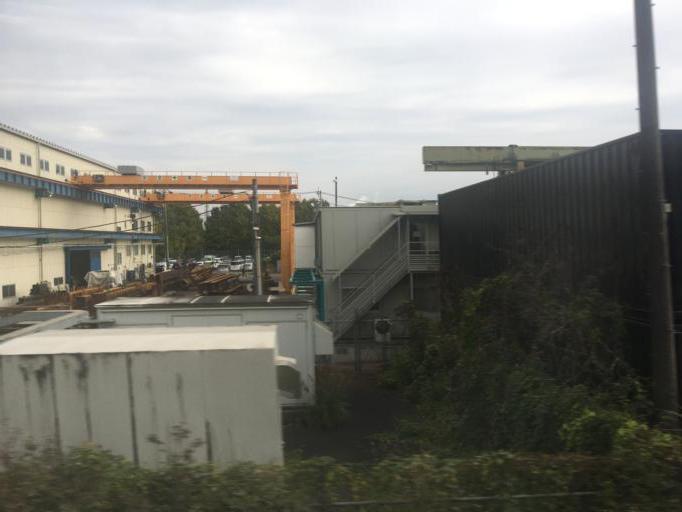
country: JP
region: Tokyo
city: Fussa
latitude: 35.7898
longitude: 139.3392
